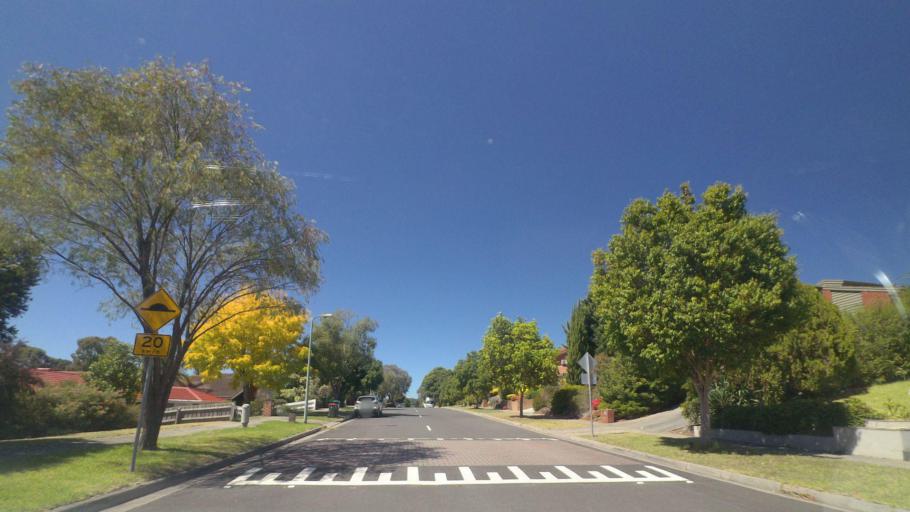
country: AU
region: Victoria
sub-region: Manningham
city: Donvale
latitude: -37.7654
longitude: 145.1758
